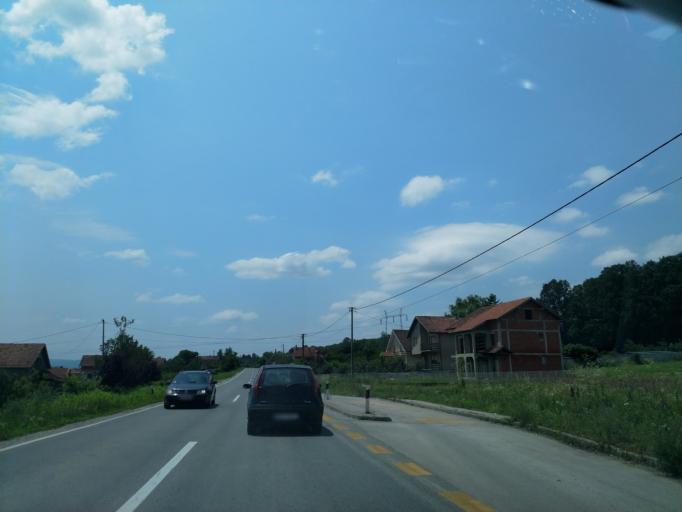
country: RS
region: Central Serbia
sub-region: Rasinski Okrug
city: Krusevac
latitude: 43.5318
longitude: 21.3199
